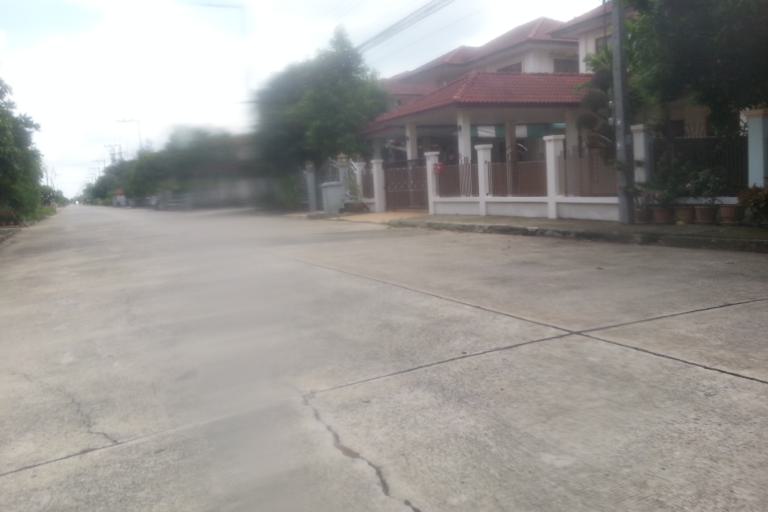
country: TH
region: Pathum Thani
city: Nong Suea
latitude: 14.0532
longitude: 100.8600
